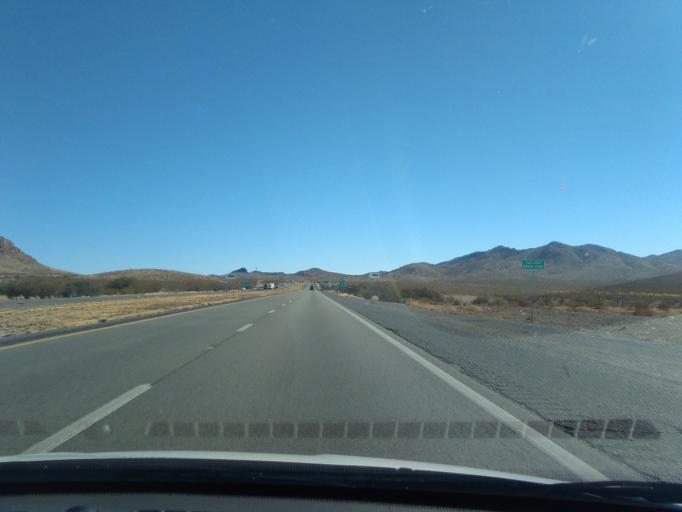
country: US
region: New Mexico
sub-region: Hidalgo County
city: Lordsburg
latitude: 32.2267
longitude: -109.0465
